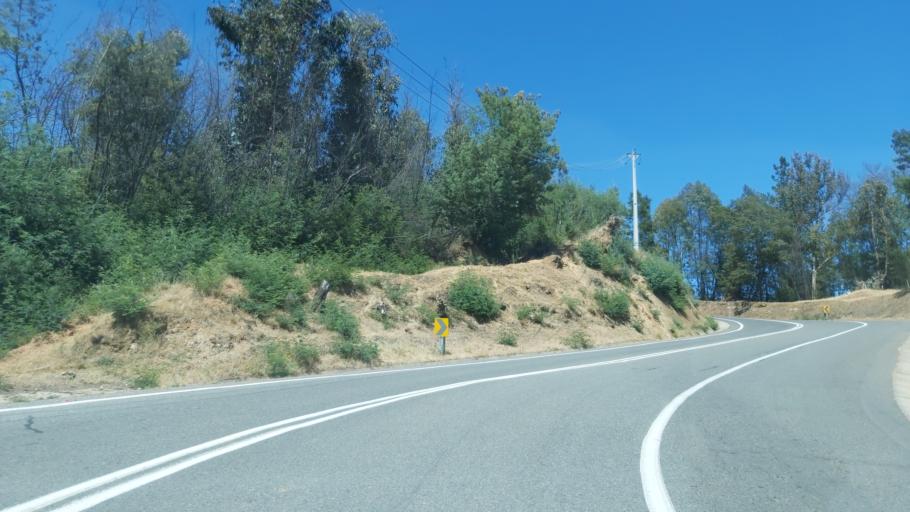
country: CL
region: Maule
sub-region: Provincia de Talca
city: Constitucion
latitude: -34.9082
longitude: -71.9958
